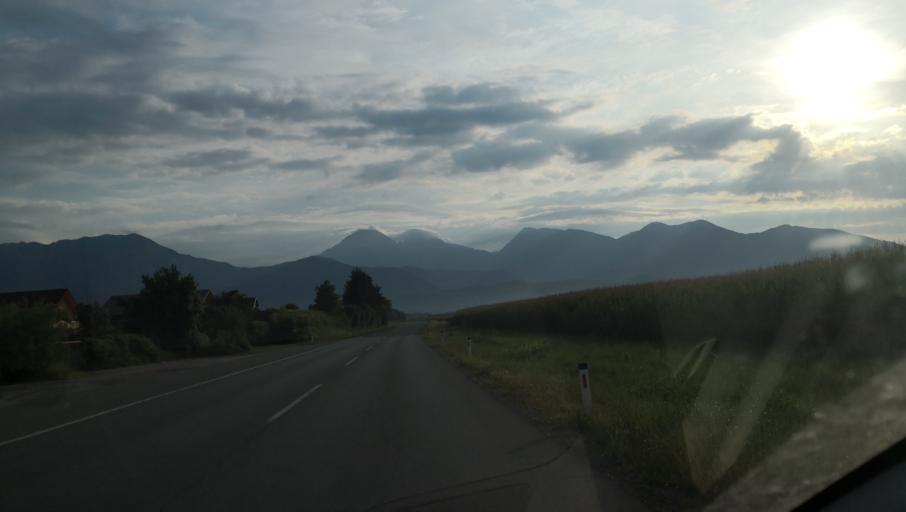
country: SI
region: Kranj
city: Britof
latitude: 46.2551
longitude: 14.3883
